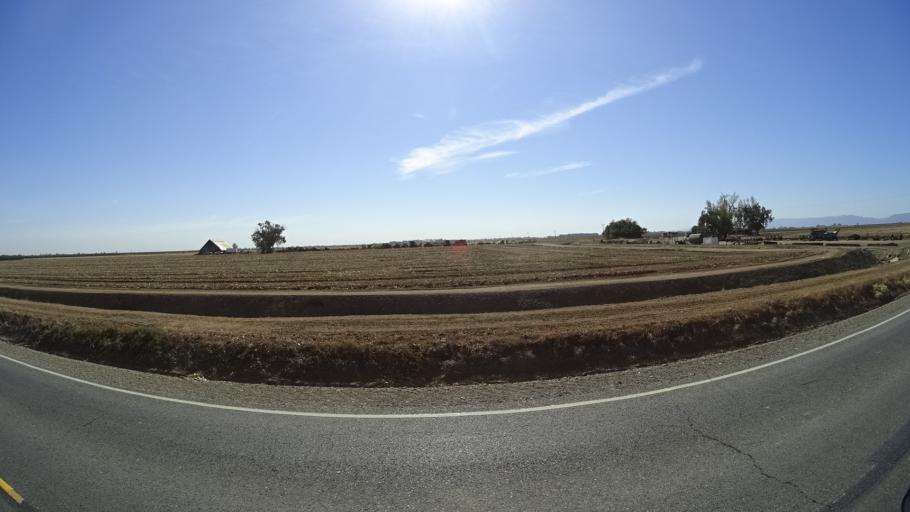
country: US
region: California
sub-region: Yolo County
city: Woodland
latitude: 38.6199
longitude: -121.8390
